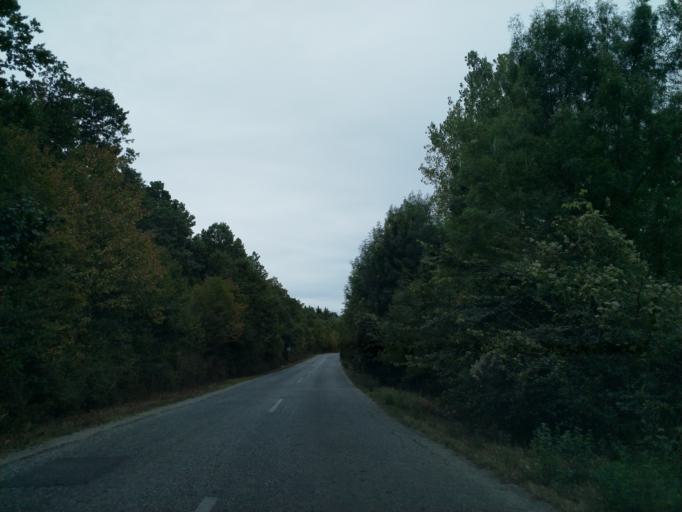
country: RS
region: Central Serbia
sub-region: Pomoravski Okrug
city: Jagodina
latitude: 44.0320
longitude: 21.1940
